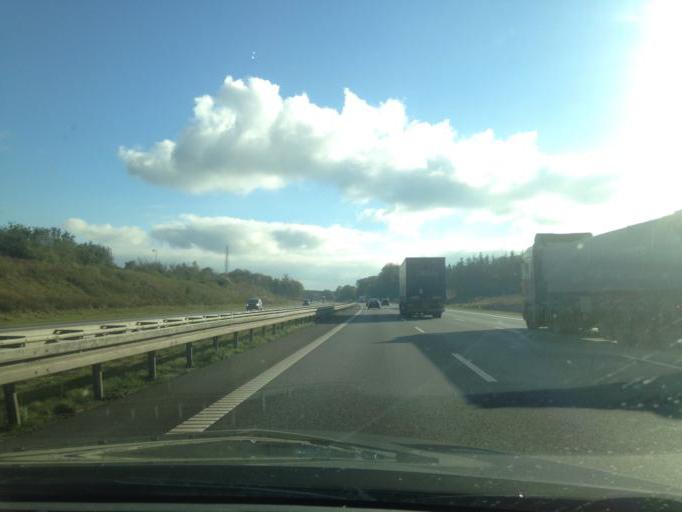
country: DK
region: South Denmark
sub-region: Vejle Kommune
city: Vejle
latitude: 55.6398
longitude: 9.5609
